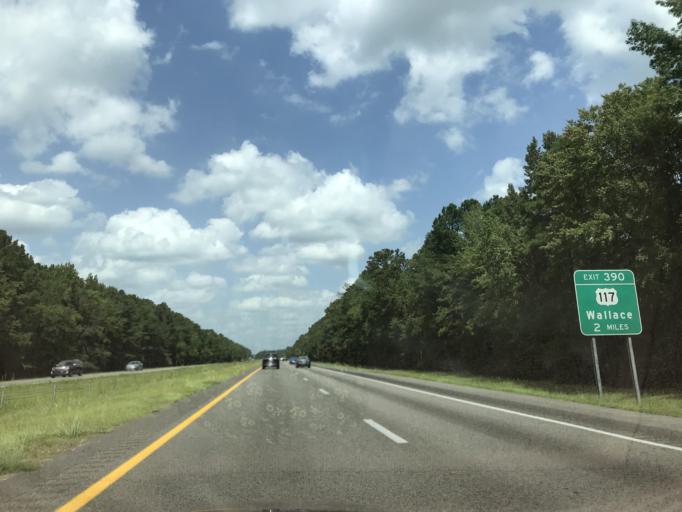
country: US
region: North Carolina
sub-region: Duplin County
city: Wallace
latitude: 34.6548
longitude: -77.9415
